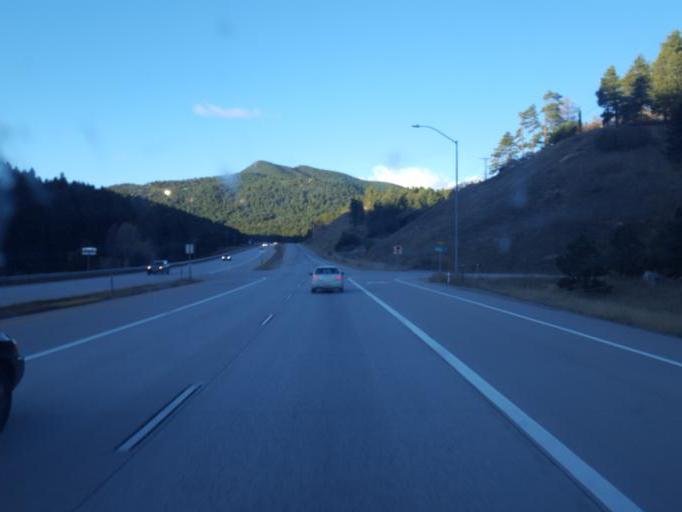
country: US
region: Colorado
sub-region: Jefferson County
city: Indian Hills
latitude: 39.5824
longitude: -105.2291
